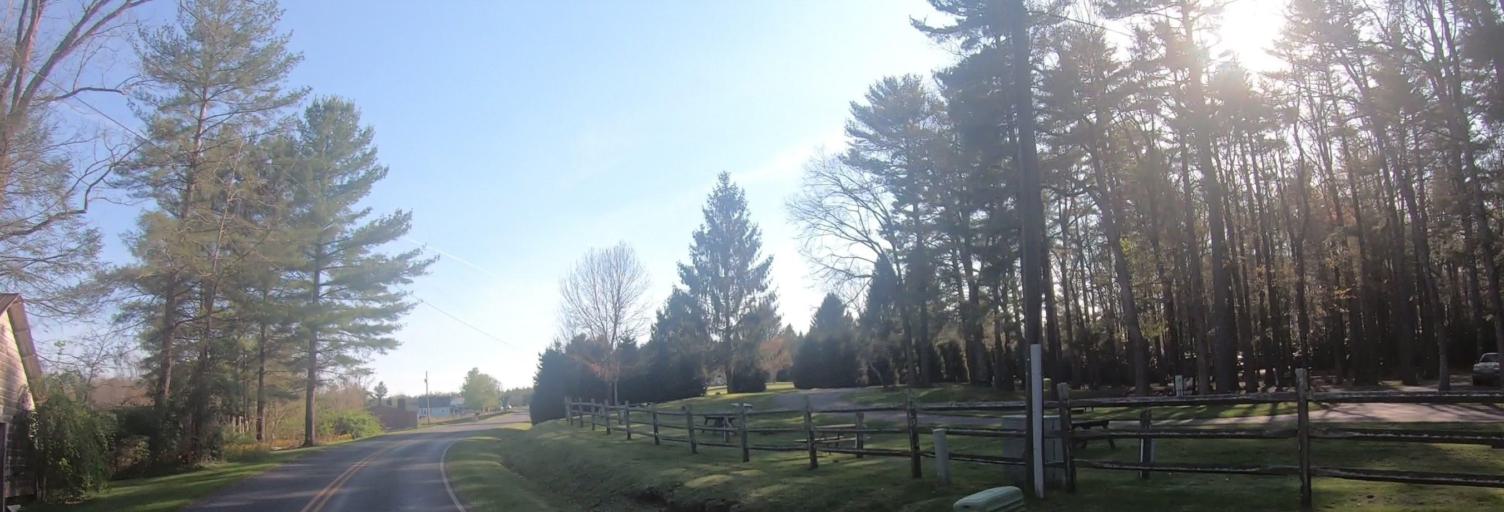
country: US
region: North Carolina
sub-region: Ashe County
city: Jefferson
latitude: 36.3556
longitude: -81.3750
